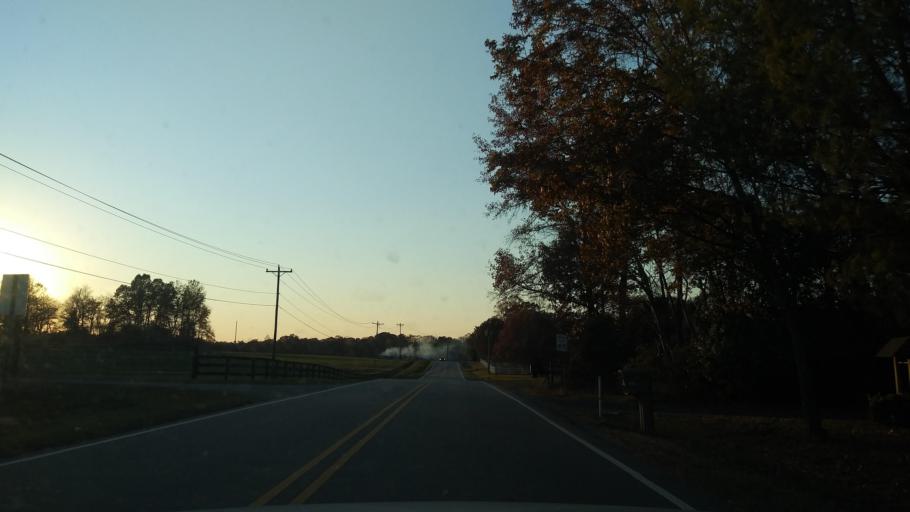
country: US
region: North Carolina
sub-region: Guilford County
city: Pleasant Garden
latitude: 35.9908
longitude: -79.7855
